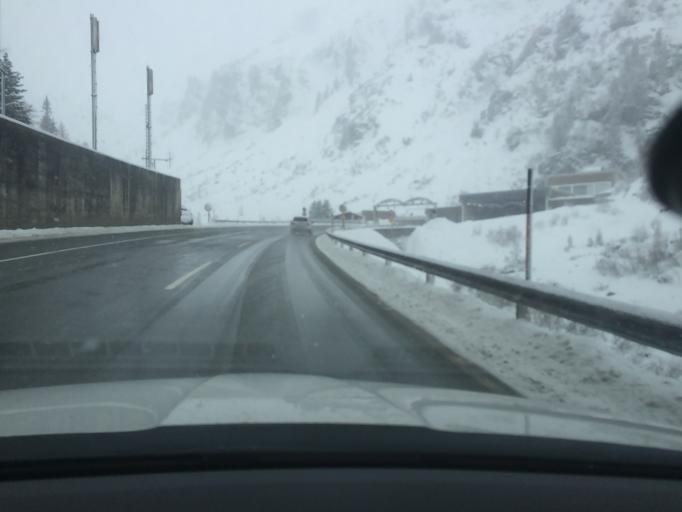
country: AT
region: Salzburg
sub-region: Politischer Bezirk Zell am See
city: Stuhlfelden
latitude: 47.1621
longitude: 12.5375
